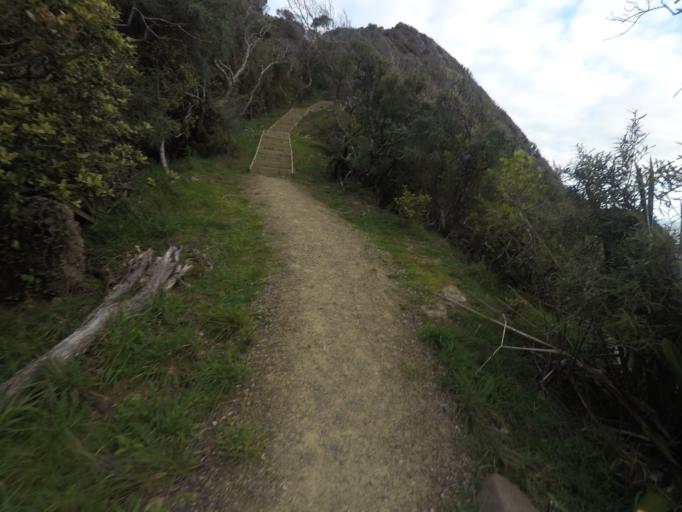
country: NZ
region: Auckland
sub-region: Auckland
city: Muriwai Beach
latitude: -36.9799
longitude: 174.4721
